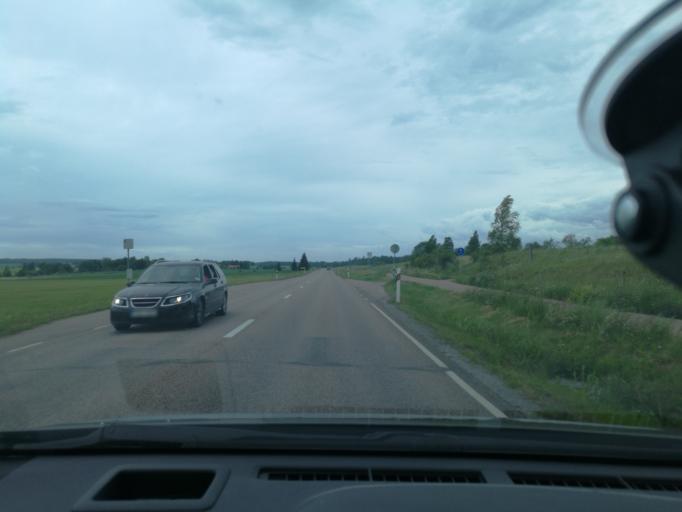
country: SE
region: Vaestmanland
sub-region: Vasteras
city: Skultuna
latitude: 59.6786
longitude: 16.4663
